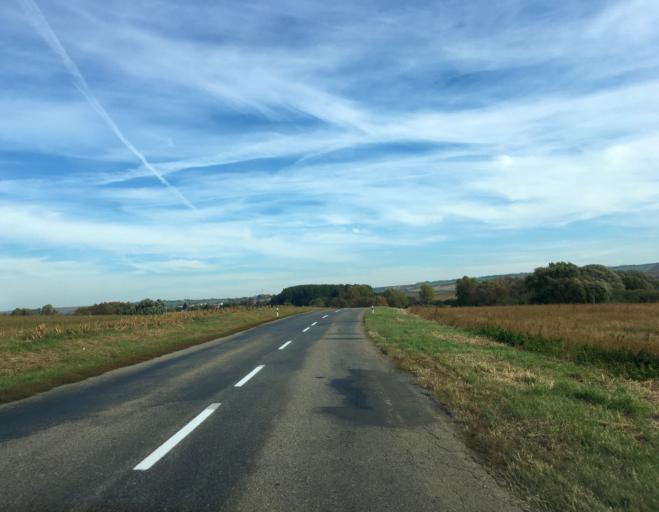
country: SK
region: Nitriansky
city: Svodin
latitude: 47.9982
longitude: 18.4091
